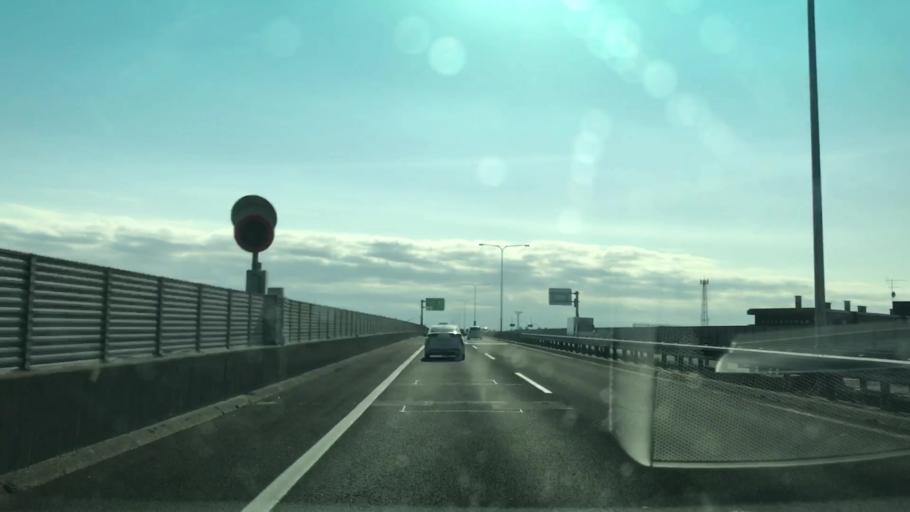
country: JP
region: Hokkaido
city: Sapporo
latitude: 43.0518
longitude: 141.4306
